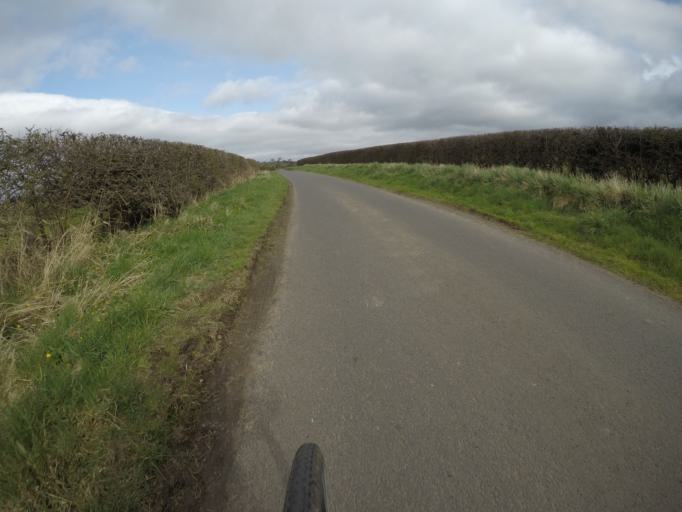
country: GB
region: Scotland
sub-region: North Ayrshire
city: Irvine
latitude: 55.6401
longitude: -4.6296
